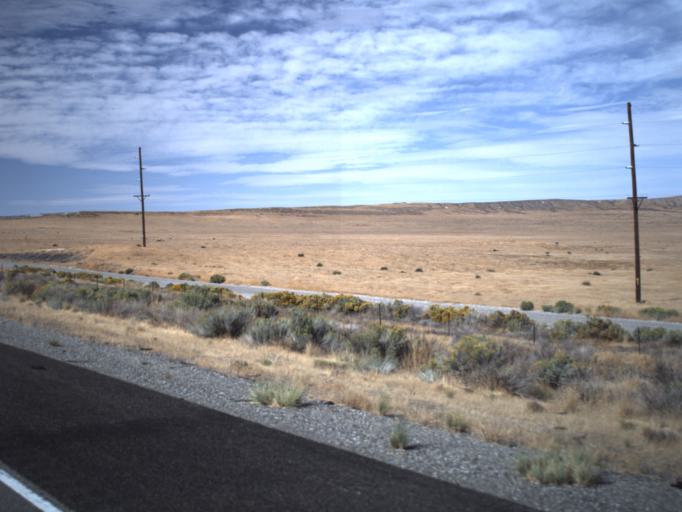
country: US
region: Utah
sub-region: Tooele County
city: Grantsville
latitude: 40.7772
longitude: -112.9727
